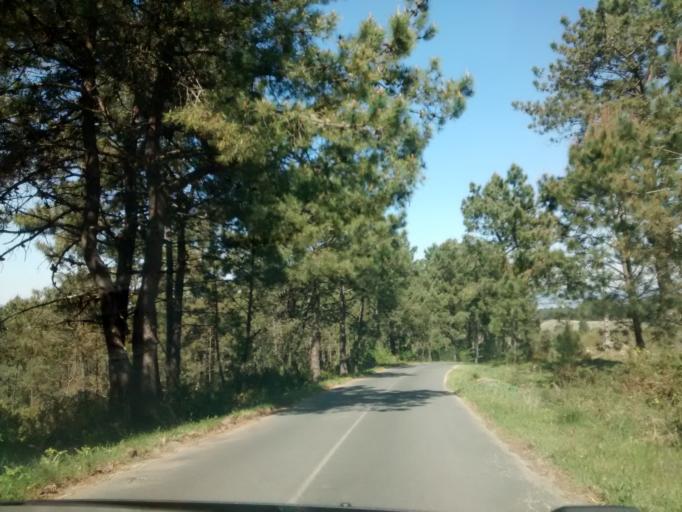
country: ES
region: Galicia
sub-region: Provincia de Pontevedra
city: O Grove
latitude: 42.4719
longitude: -8.8833
